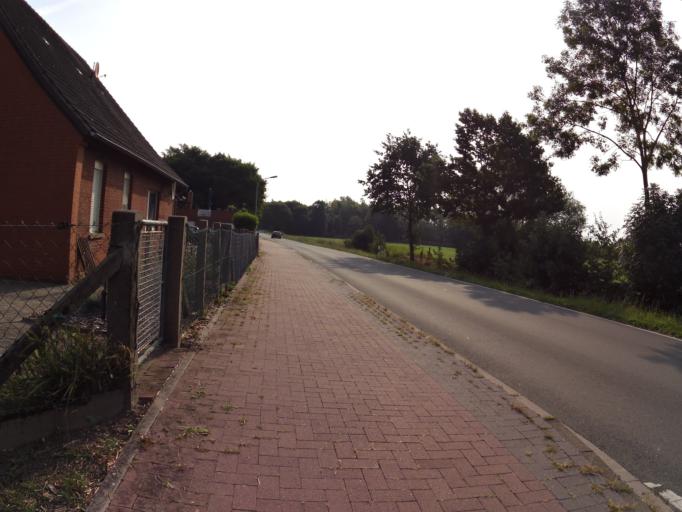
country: DE
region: Lower Saxony
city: Raddestorf
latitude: 52.4220
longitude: 8.9756
